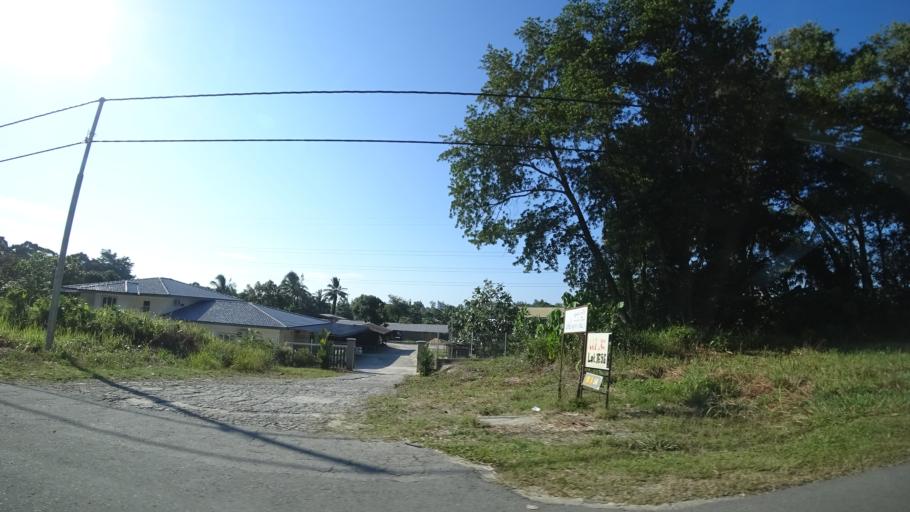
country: BN
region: Tutong
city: Tutong
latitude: 4.6988
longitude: 114.5206
